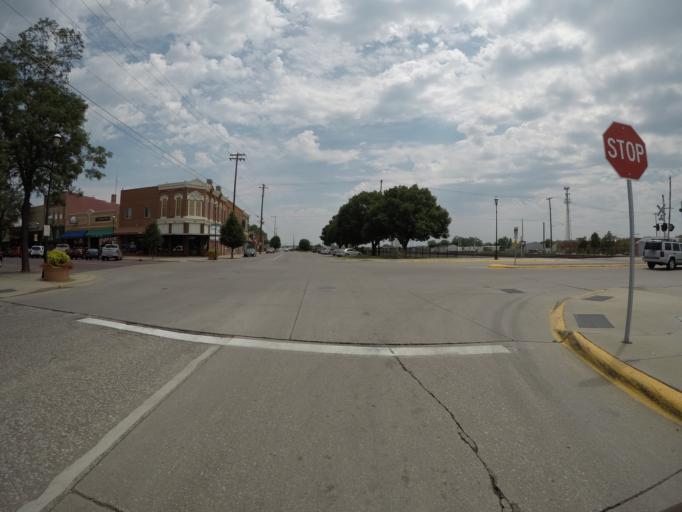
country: US
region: Nebraska
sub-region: Buffalo County
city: Kearney
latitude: 40.6952
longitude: -99.0820
